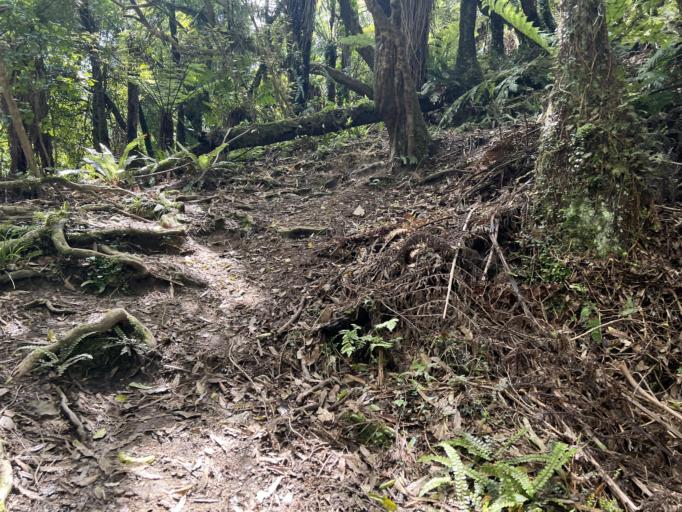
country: NZ
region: Wellington
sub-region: Kapiti Coast District
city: Paraparaumu
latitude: -40.8790
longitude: 175.0912
